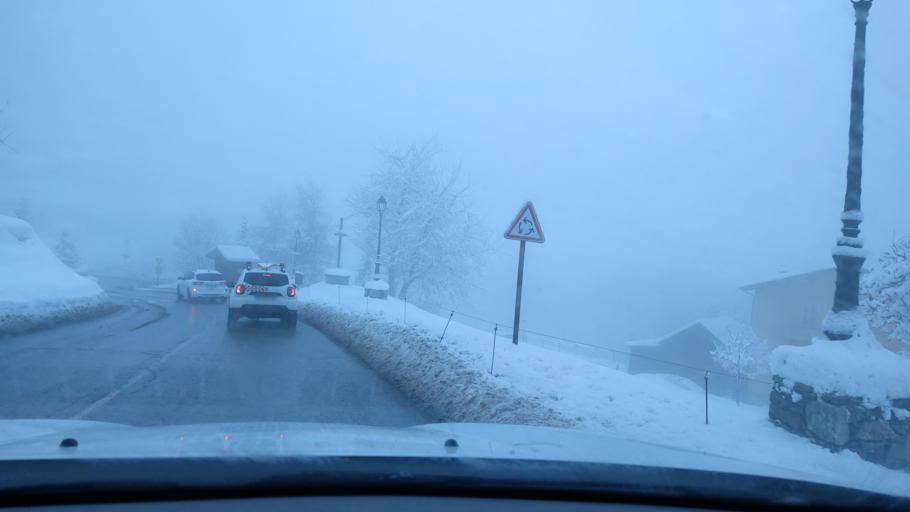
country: FR
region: Rhone-Alpes
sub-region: Departement de la Savoie
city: Saint-Bon-Tarentaise
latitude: 45.4354
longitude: 6.6369
